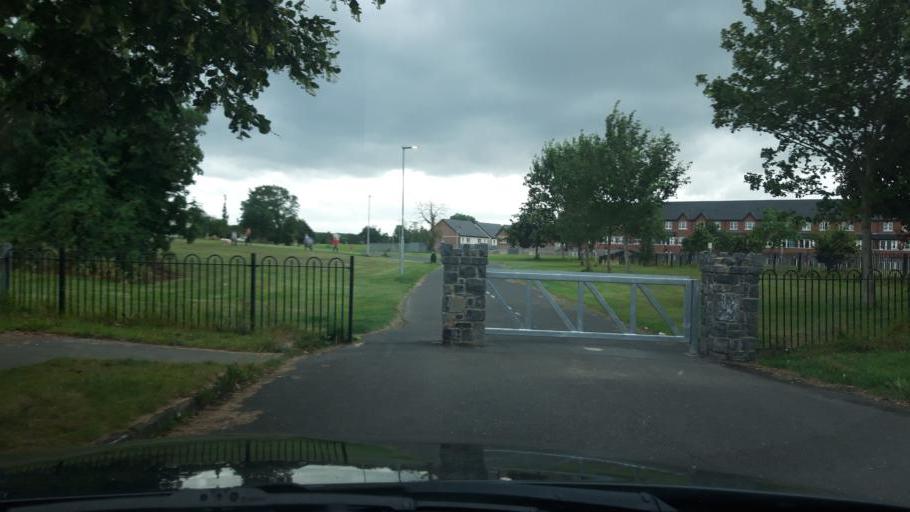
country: IE
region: Leinster
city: Hartstown
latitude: 53.4010
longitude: -6.4262
